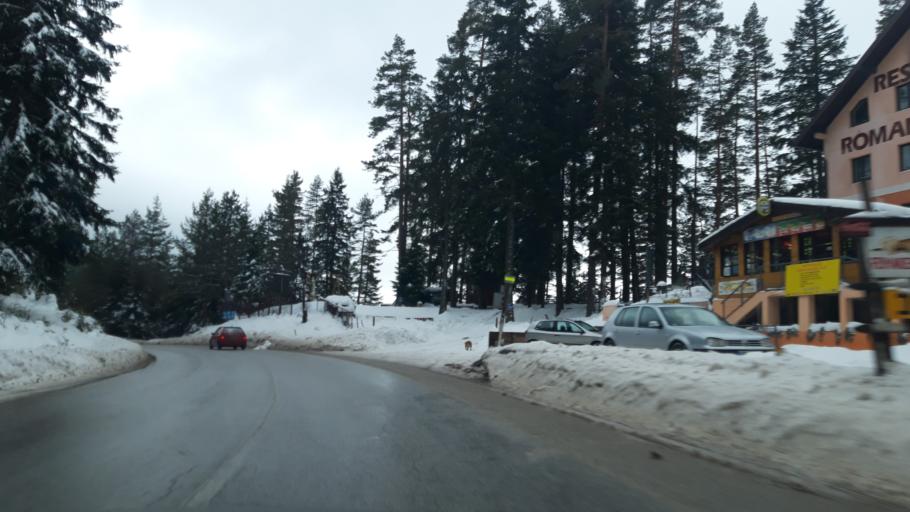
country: BA
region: Republika Srpska
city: Pale
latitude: 43.9226
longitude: 18.6512
